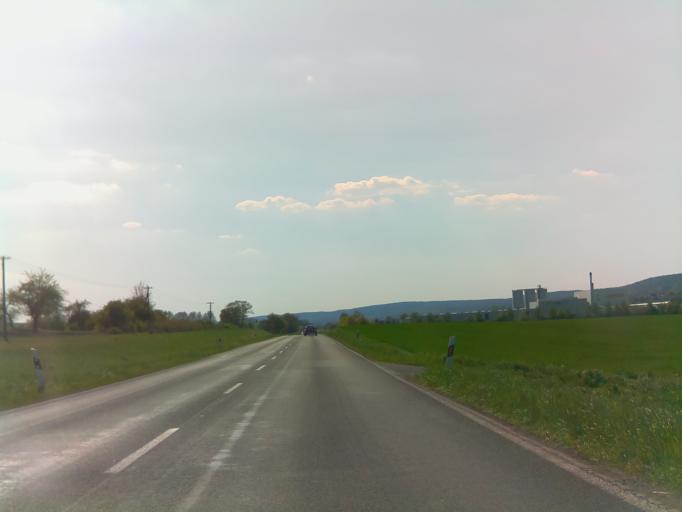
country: DE
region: Thuringia
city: Dreitzsch
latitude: 50.7382
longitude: 11.7912
